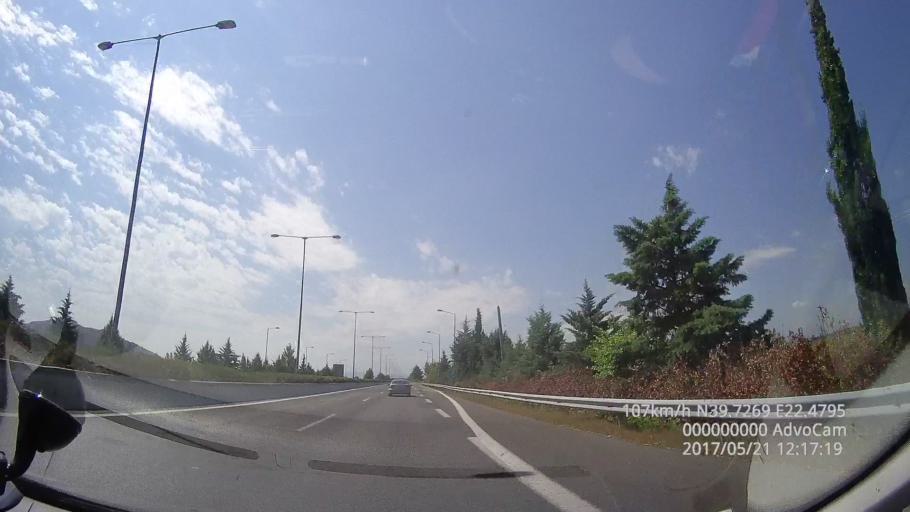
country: GR
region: Thessaly
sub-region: Nomos Larisis
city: Makrychori
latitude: 39.7264
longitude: 22.4797
